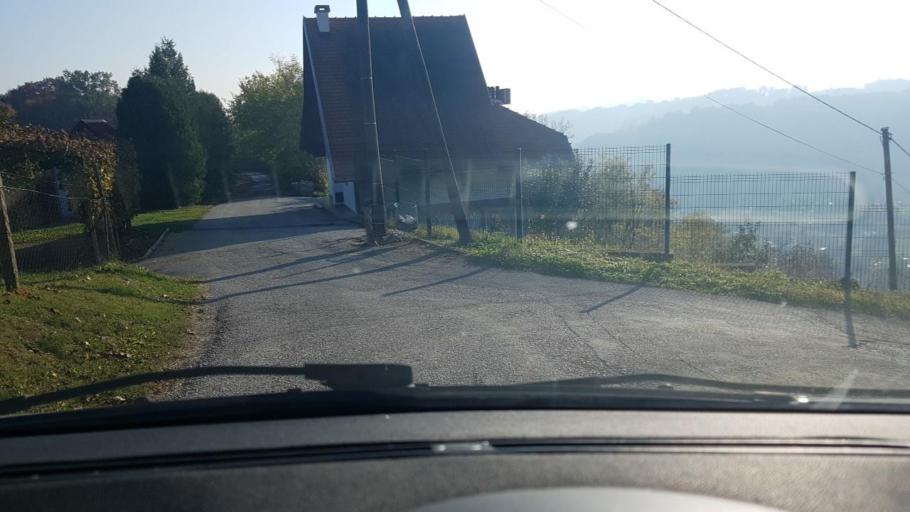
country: HR
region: Krapinsko-Zagorska
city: Zabok
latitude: 46.0346
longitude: 15.8867
